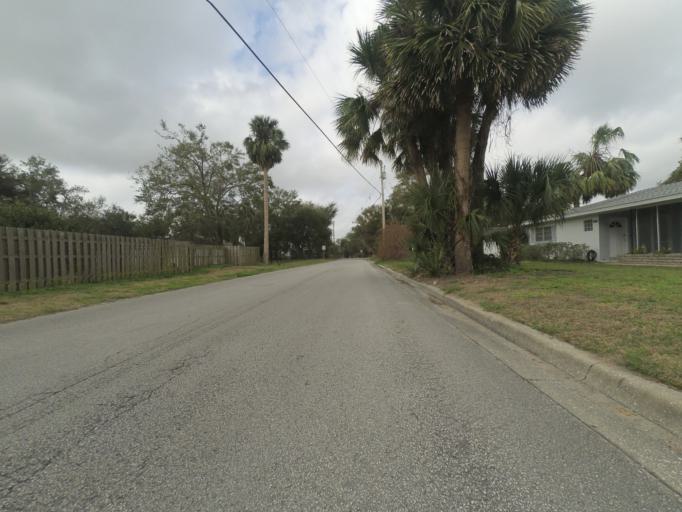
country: US
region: Florida
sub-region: Lake County
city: Umatilla
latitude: 28.9242
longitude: -81.6648
